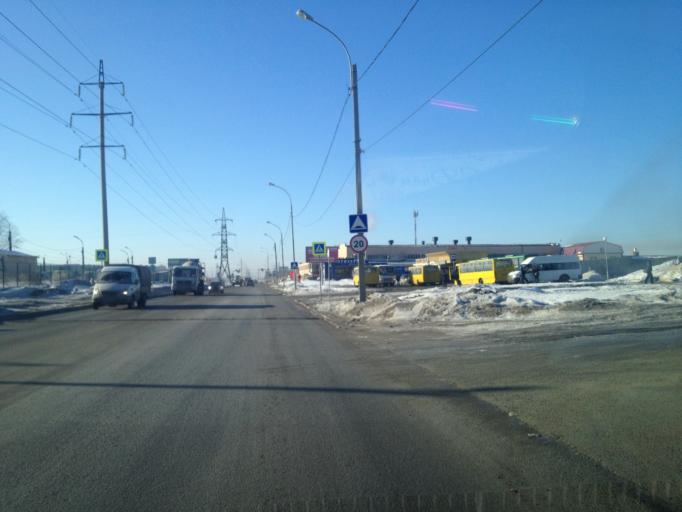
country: RU
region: Sverdlovsk
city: Sovkhoznyy
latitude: 56.7595
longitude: 60.5886
